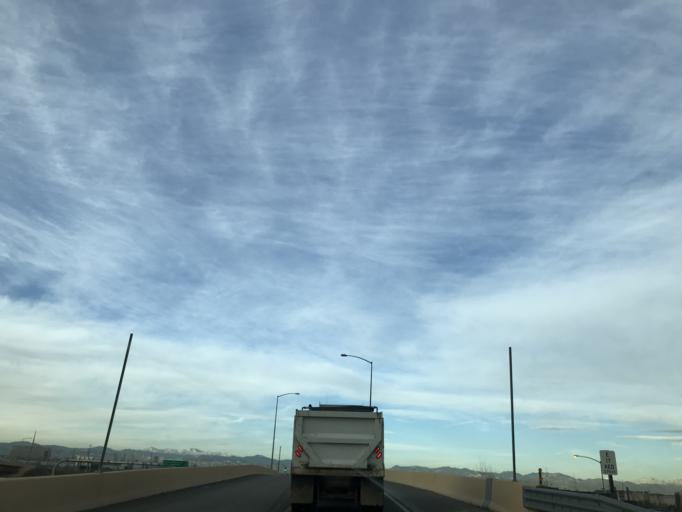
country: US
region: Colorado
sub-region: Adams County
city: Commerce City
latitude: 39.7783
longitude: -104.8859
